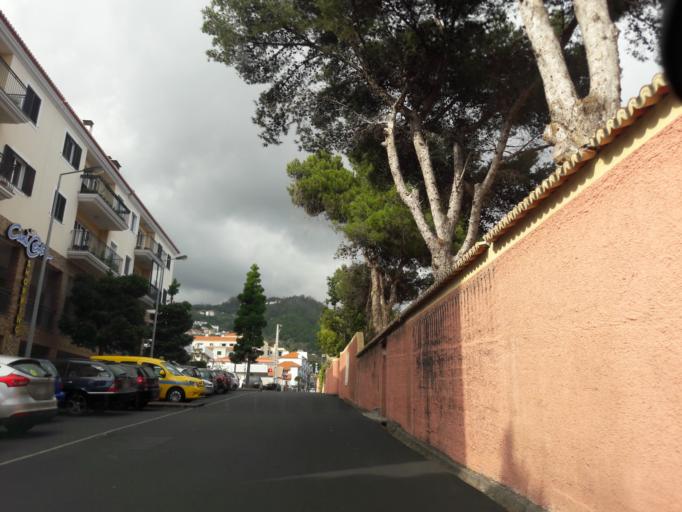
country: PT
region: Madeira
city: Canico
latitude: 32.6498
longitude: -16.8388
